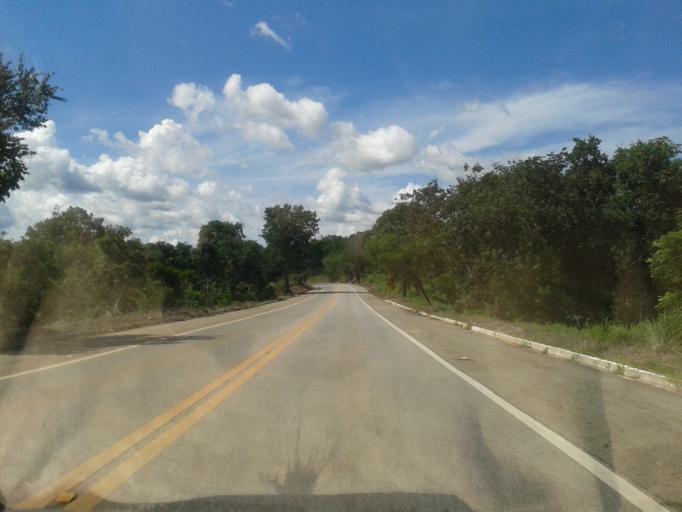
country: BR
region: Goias
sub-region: Goias
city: Goias
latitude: -15.6617
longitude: -50.2185
